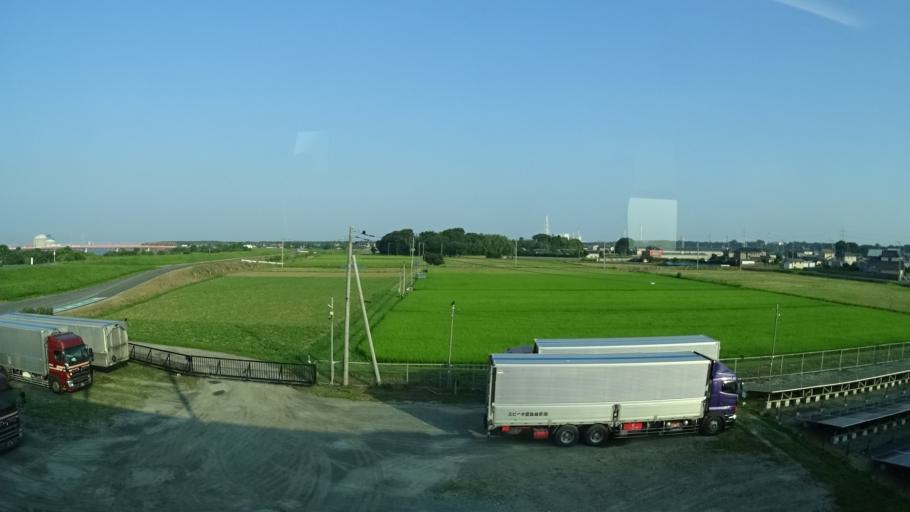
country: JP
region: Ibaraki
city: Funaishikawa
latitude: 36.4848
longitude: 140.5944
